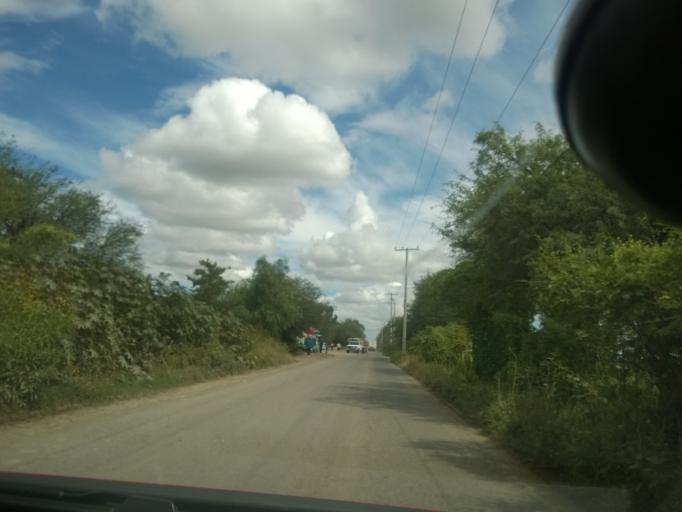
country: MX
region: Guanajuato
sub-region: Leon
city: El CERESO
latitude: 20.9970
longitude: -101.6943
